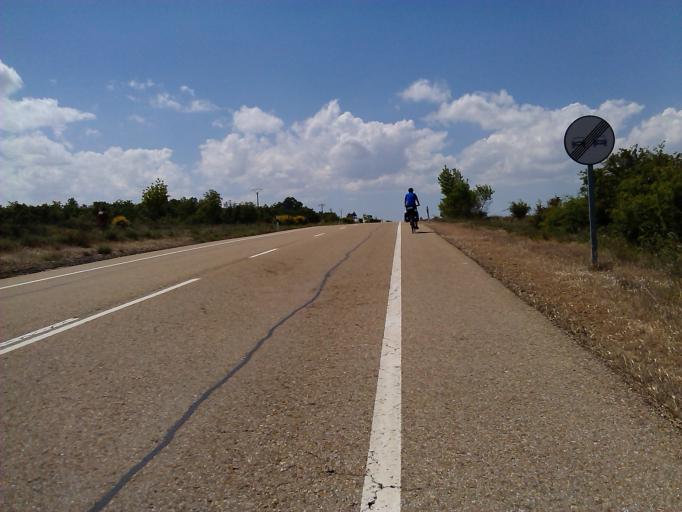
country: ES
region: Castille and Leon
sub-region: Provincia de Palencia
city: Ledigos
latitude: 42.3442
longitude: -4.8455
